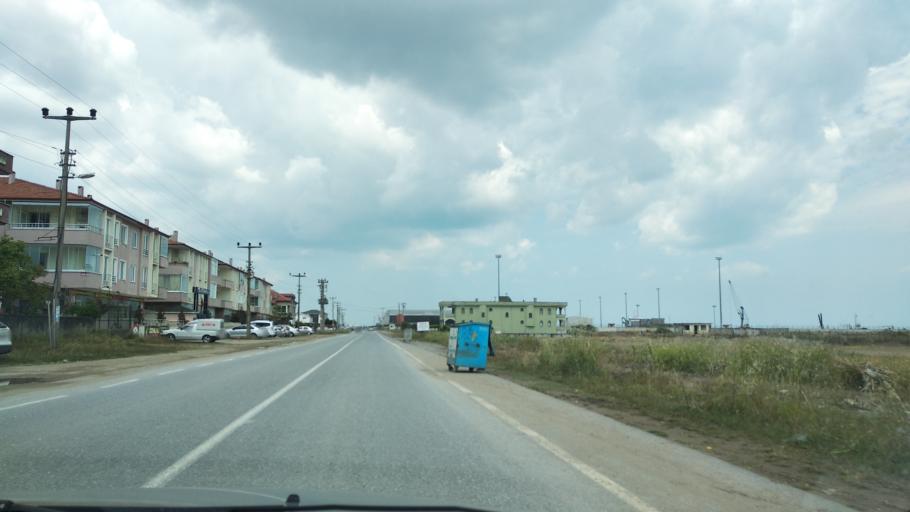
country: TR
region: Sakarya
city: Karasu
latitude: 41.1150
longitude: 30.6794
